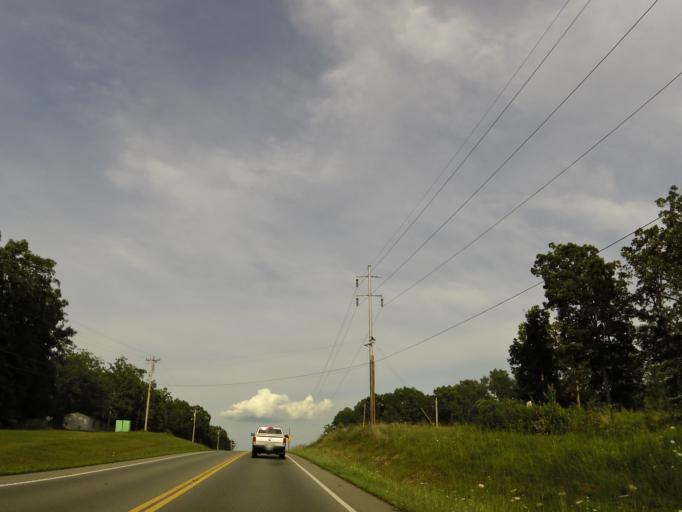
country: US
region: Tennessee
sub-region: Humphreys County
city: McEwen
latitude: 36.0942
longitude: -87.5665
